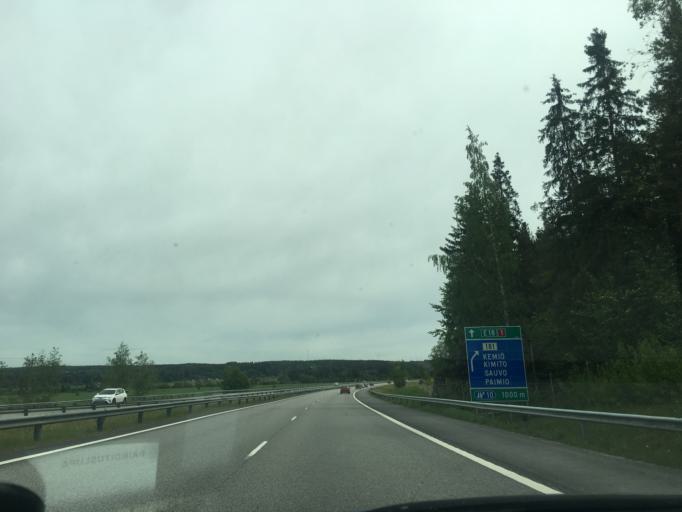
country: FI
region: Varsinais-Suomi
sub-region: Turku
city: Paimio
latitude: 60.4349
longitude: 22.6441
